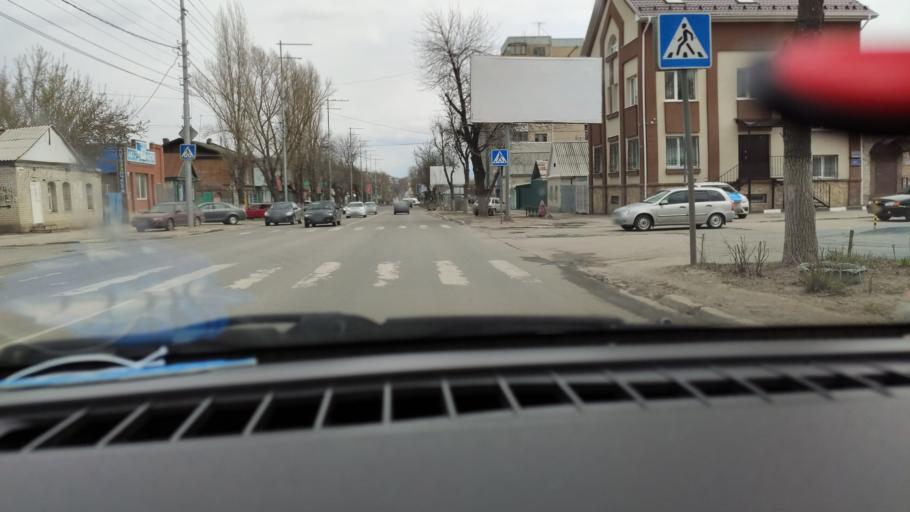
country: RU
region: Saratov
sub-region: Saratovskiy Rayon
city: Saratov
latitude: 51.5447
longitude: 46.0306
